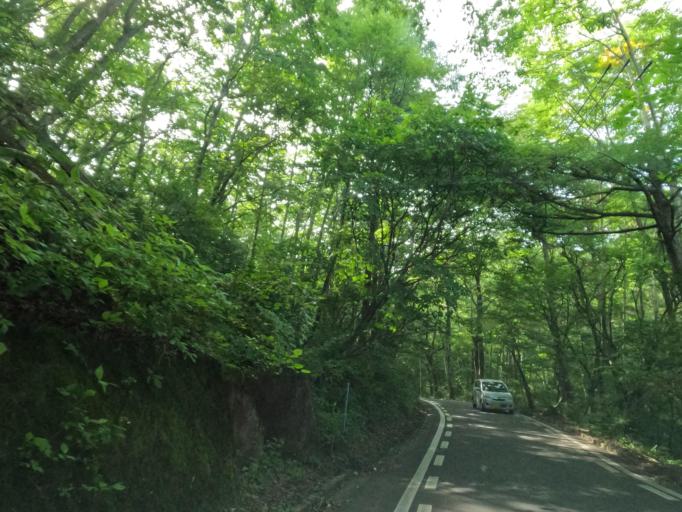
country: JP
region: Nagano
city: Komoro
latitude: 36.3580
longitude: 138.6152
